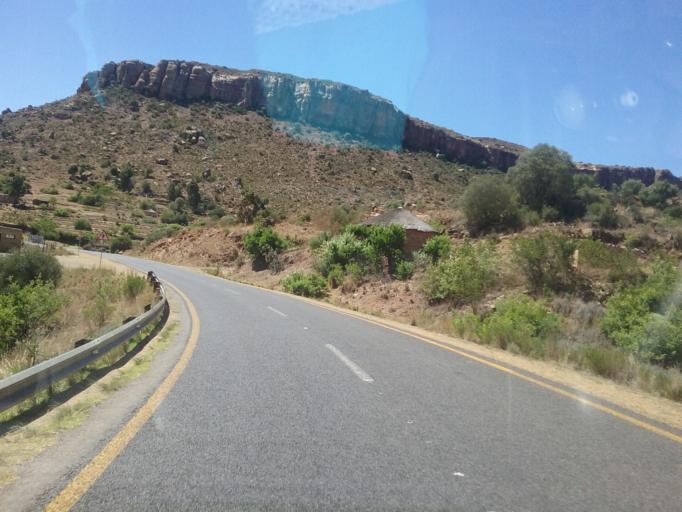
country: LS
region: Quthing
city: Quthing
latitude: -30.2937
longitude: 27.7628
